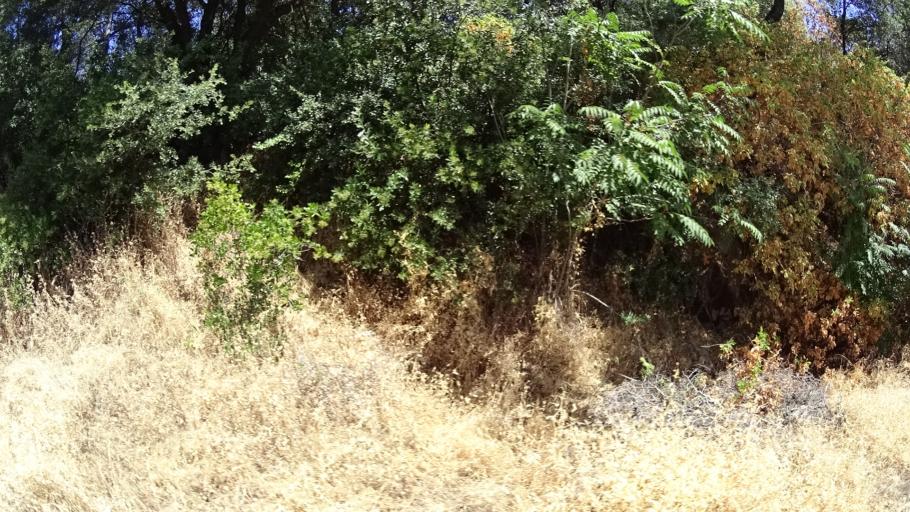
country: US
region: California
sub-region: Amador County
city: Jackson
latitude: 38.3012
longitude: -120.7111
